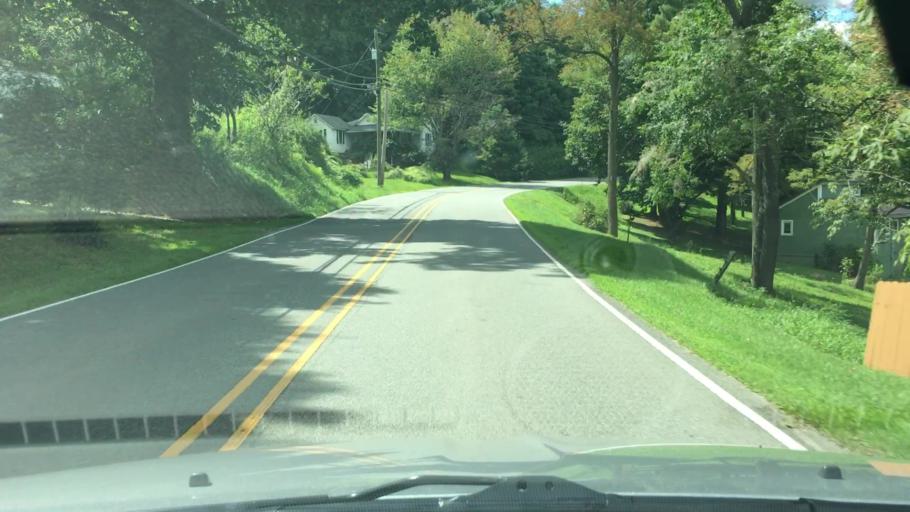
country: US
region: North Carolina
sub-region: Yancey County
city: Burnsville
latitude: 35.8695
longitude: -82.2073
